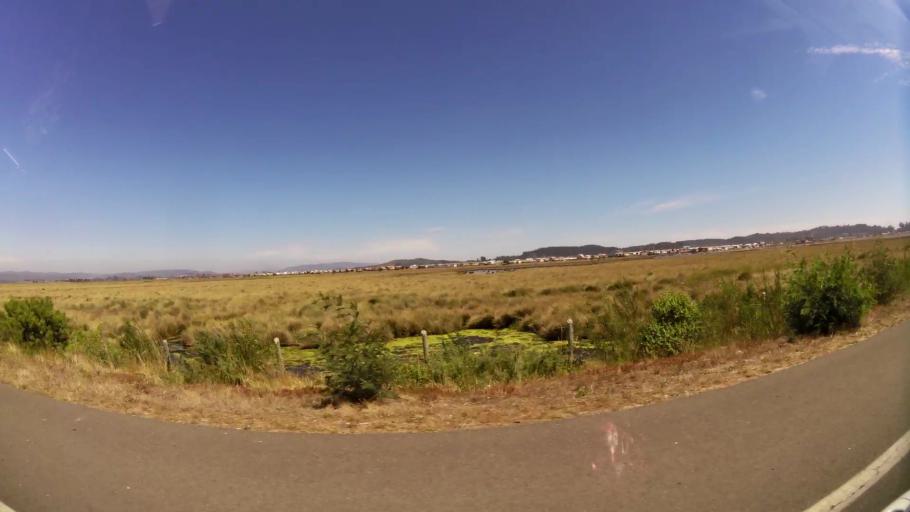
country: CL
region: Biobio
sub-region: Provincia de Concepcion
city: Talcahuano
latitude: -36.7333
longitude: -73.0856
